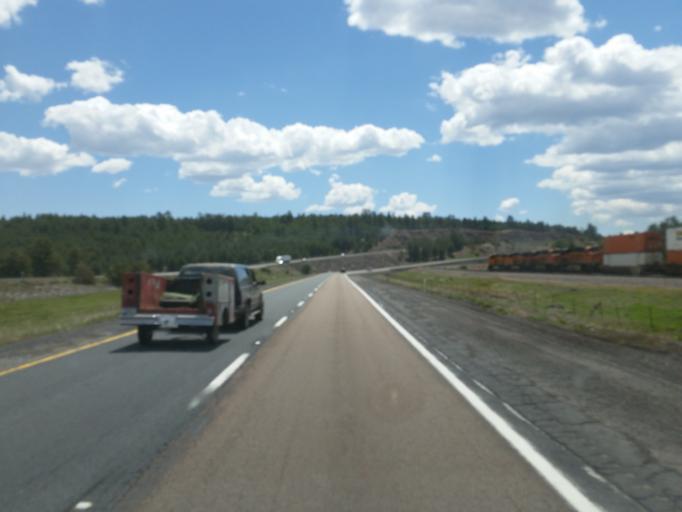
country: US
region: Arizona
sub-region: Coconino County
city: Flagstaff
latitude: 35.2136
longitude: -111.7793
